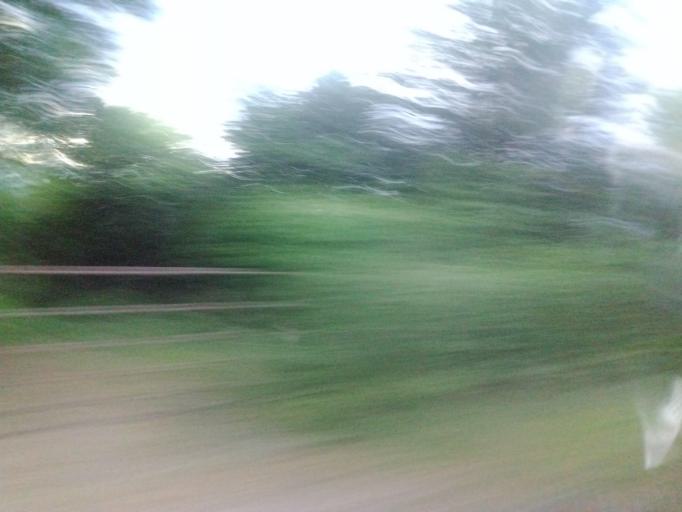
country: IE
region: Leinster
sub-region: Laois
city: Mountmellick
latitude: 53.1293
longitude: -7.3749
